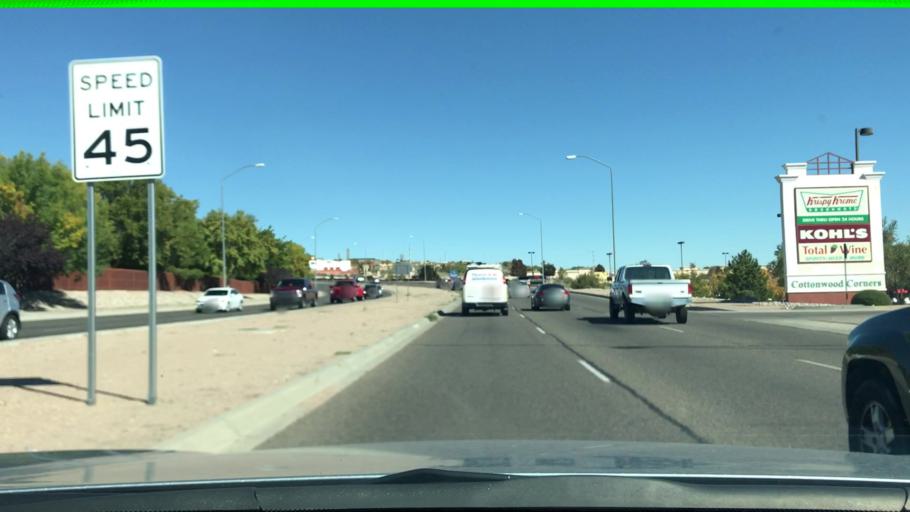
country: US
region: New Mexico
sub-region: Sandoval County
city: Rio Rancho
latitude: 35.2069
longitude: -106.6587
